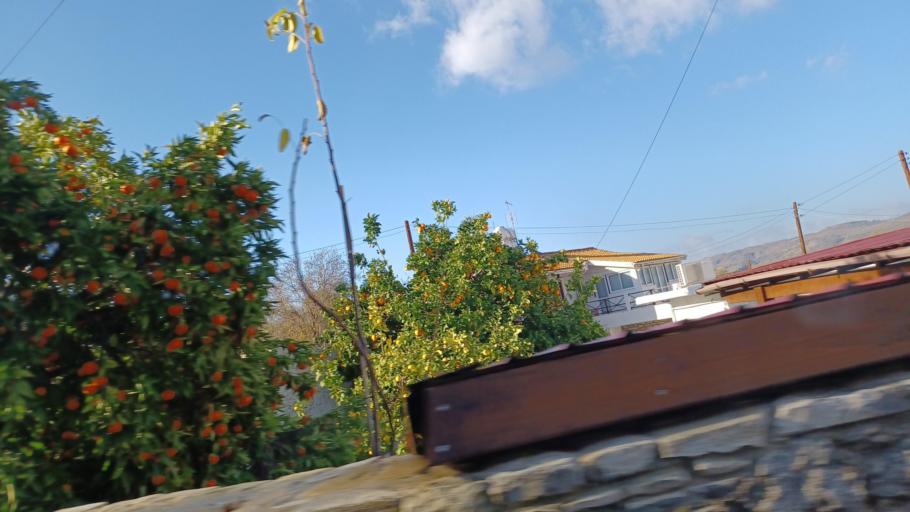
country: CY
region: Limassol
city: Pachna
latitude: 34.8518
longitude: 32.7431
